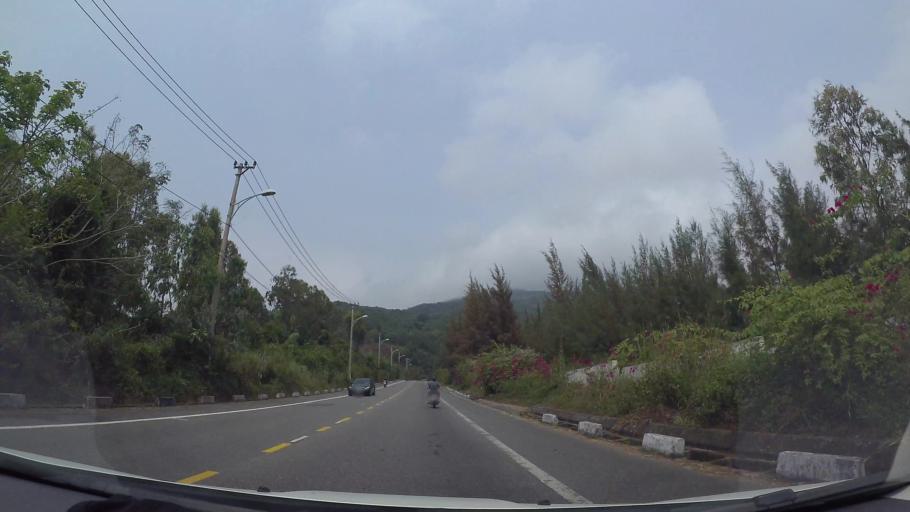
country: VN
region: Da Nang
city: Son Tra
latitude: 16.0989
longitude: 108.2695
